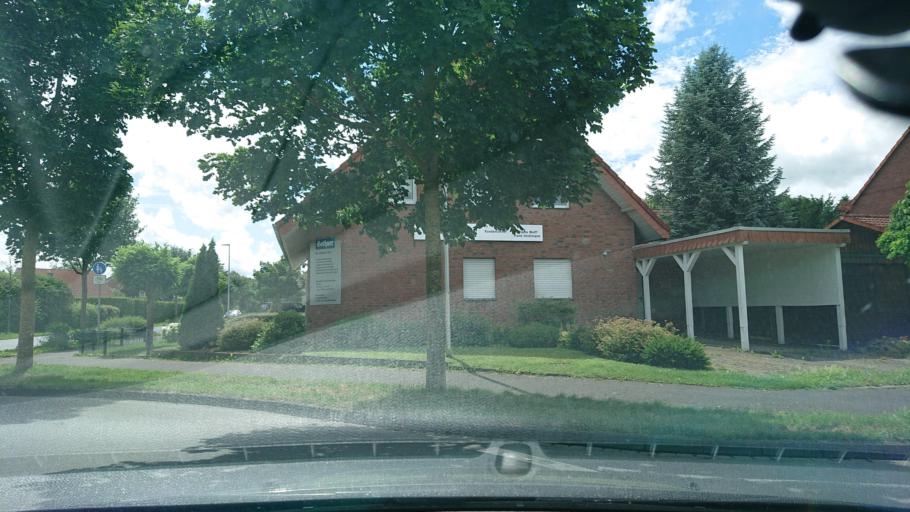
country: DE
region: North Rhine-Westphalia
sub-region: Regierungsbezirk Arnsberg
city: Soest
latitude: 51.5605
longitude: 8.0948
